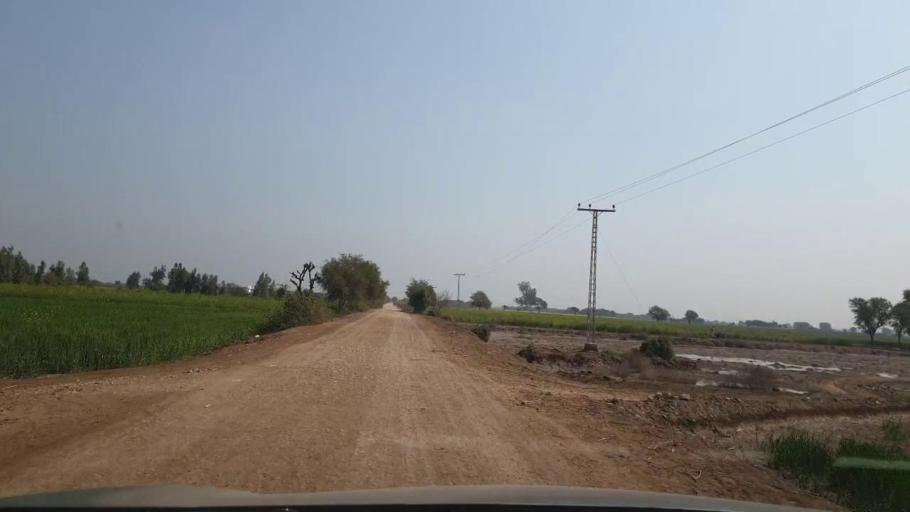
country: PK
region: Sindh
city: Tando Allahyar
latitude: 25.5374
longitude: 68.7999
